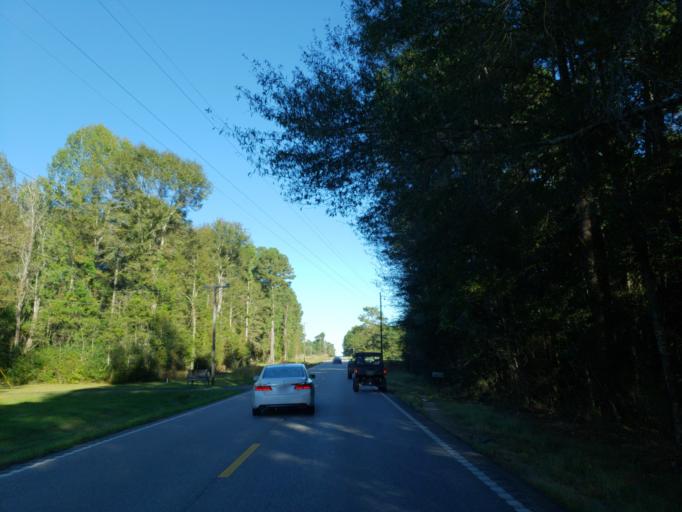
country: US
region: Mississippi
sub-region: Perry County
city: Richton
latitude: 31.3578
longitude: -89.0171
